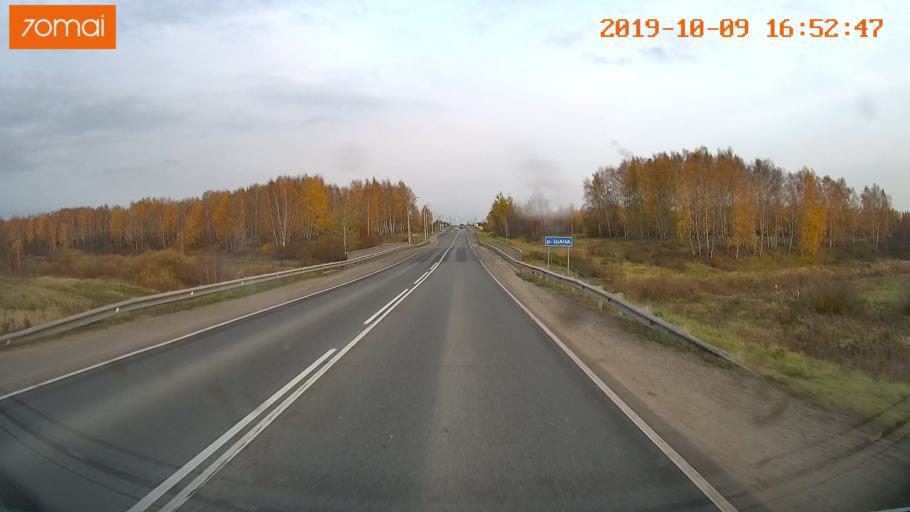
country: RU
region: Ivanovo
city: Privolzhsk
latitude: 57.3790
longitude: 41.2559
